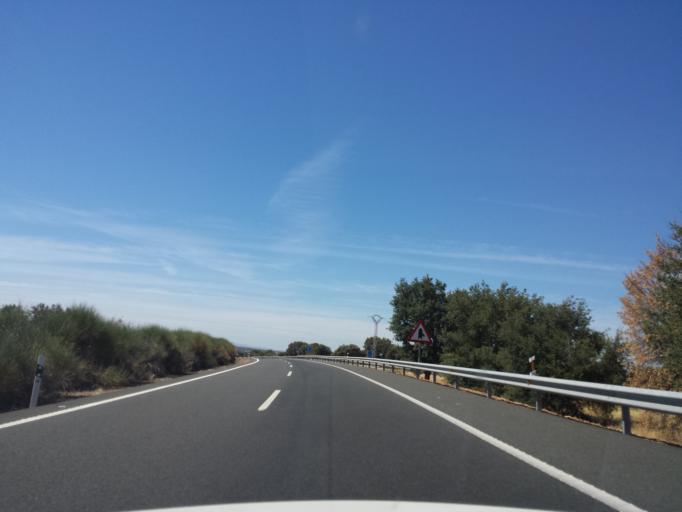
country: ES
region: Extremadura
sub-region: Provincia de Caceres
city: Jaraicejo
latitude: 39.6295
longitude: -5.8220
